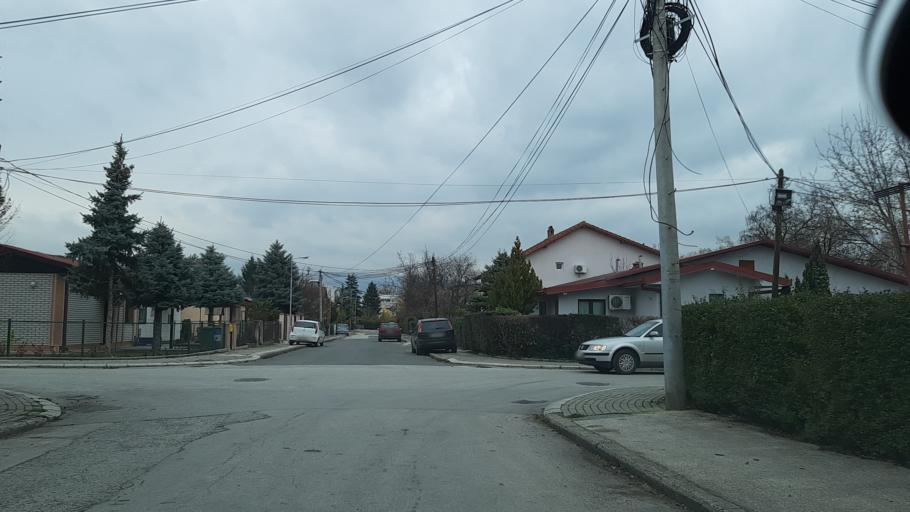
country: MK
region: Kisela Voda
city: Usje
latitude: 41.9760
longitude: 21.4707
